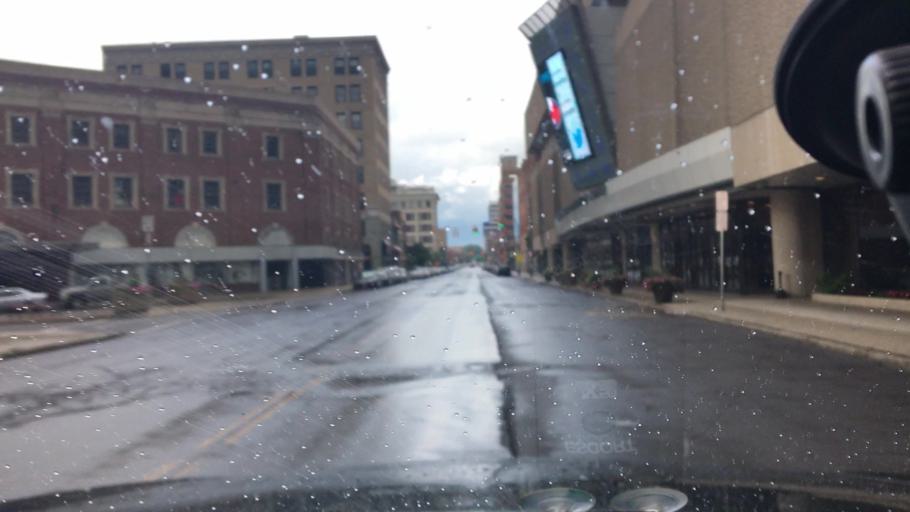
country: US
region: New York
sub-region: Erie County
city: Buffalo
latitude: 42.8867
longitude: -78.8764
